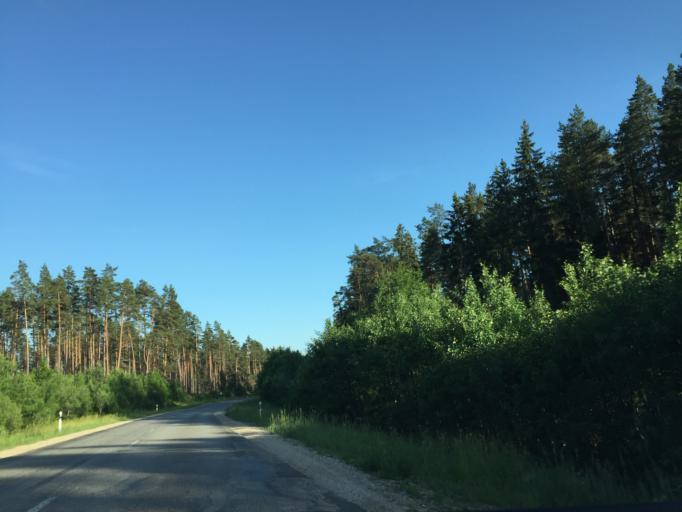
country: LV
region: Tukuma Rajons
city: Tukums
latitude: 57.0058
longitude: 23.1431
